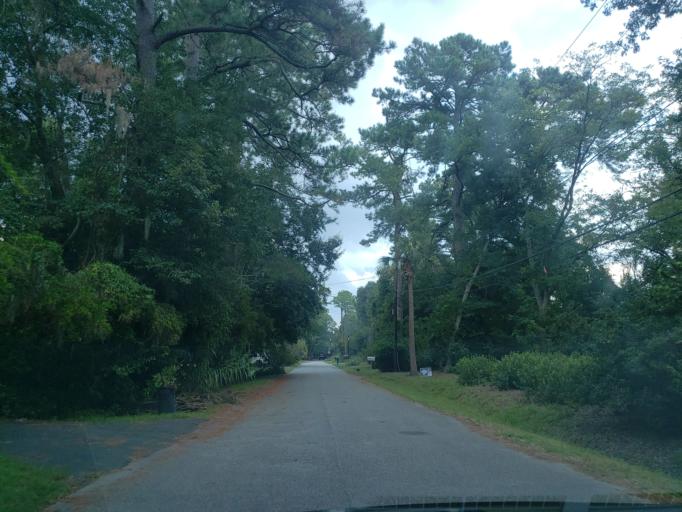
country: US
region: Georgia
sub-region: Chatham County
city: Isle of Hope
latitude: 31.9924
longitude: -81.0627
